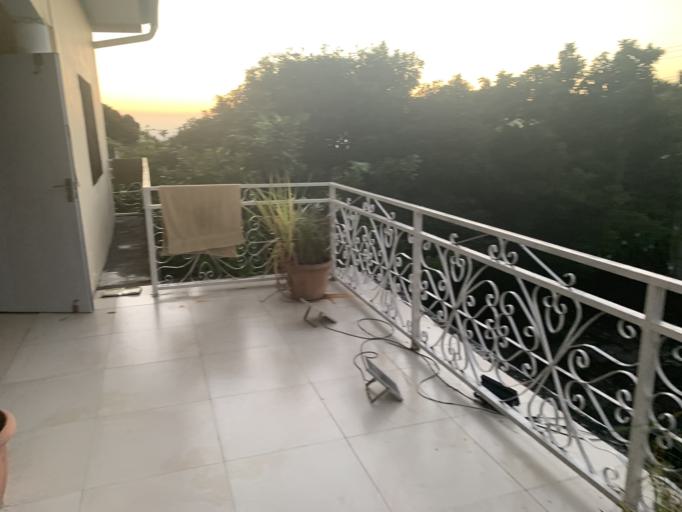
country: KM
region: Grande Comore
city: Mavingouni
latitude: -11.7341
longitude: 43.2584
